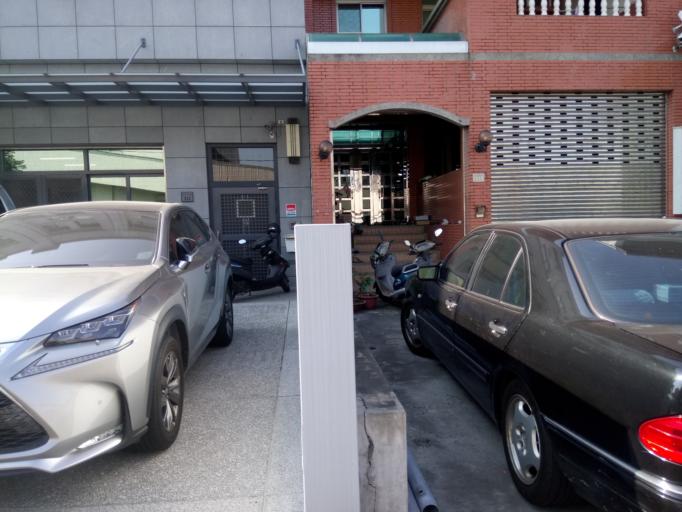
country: TW
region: Taiwan
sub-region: Changhua
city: Chang-hua
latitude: 24.0793
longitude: 120.5353
